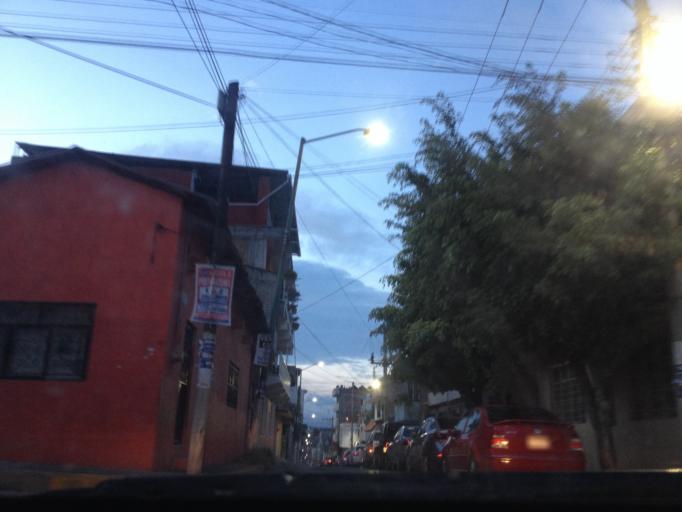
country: MX
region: Guerrero
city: Chilpancingo de los Bravos
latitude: 17.5564
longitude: -99.5005
